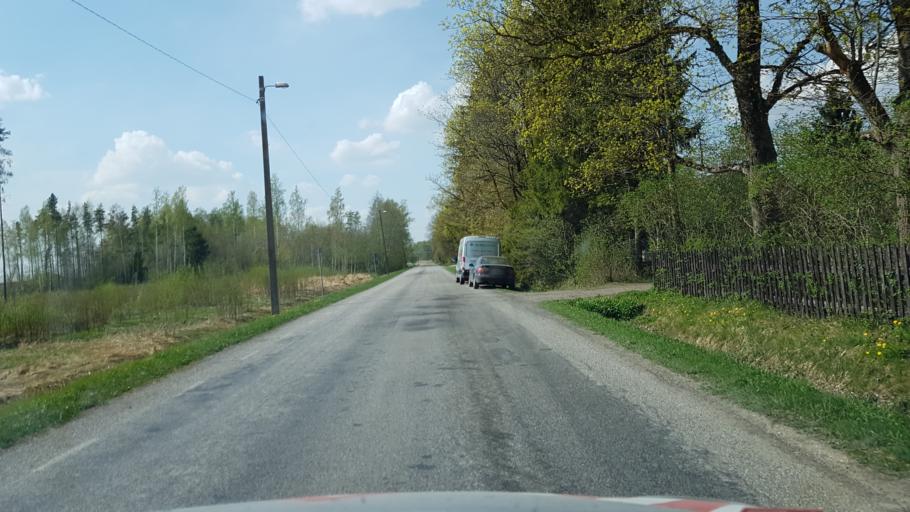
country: EE
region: Paernumaa
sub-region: Sindi linn
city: Sindi
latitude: 58.4276
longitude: 24.6499
